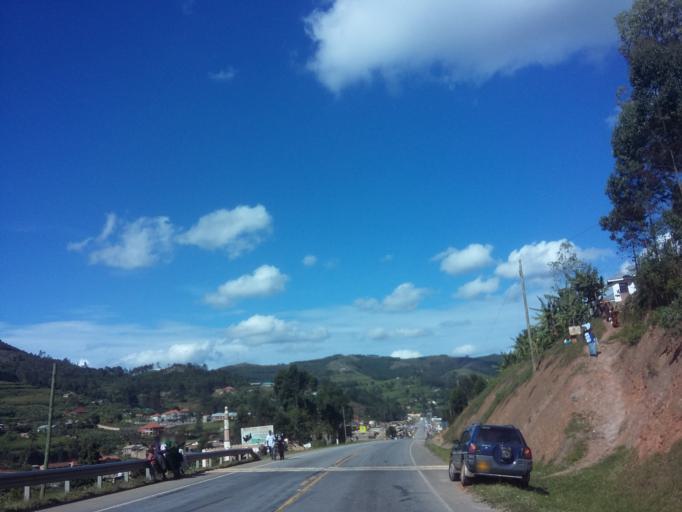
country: UG
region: Western Region
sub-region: Kabale District
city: Kabale
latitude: -1.1712
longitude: 30.1175
